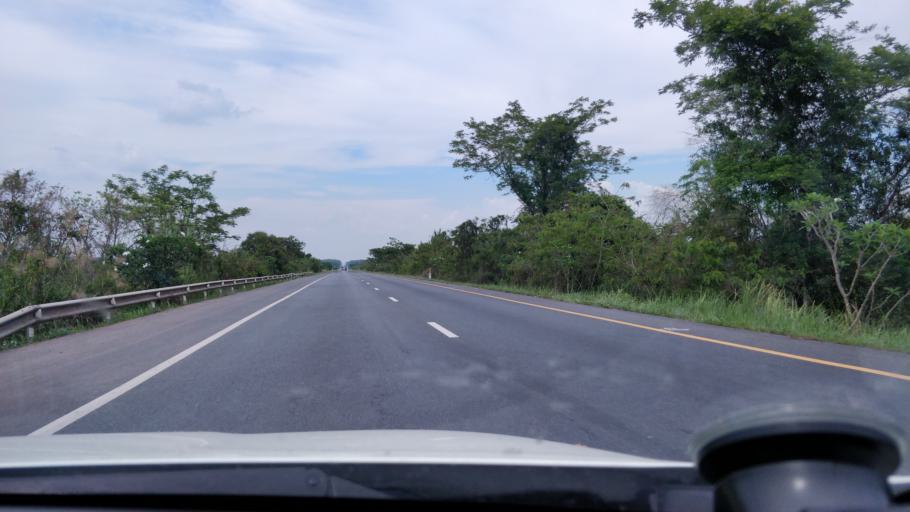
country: TH
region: Surat Thani
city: Khian Sa
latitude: 8.8573
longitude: 99.1867
